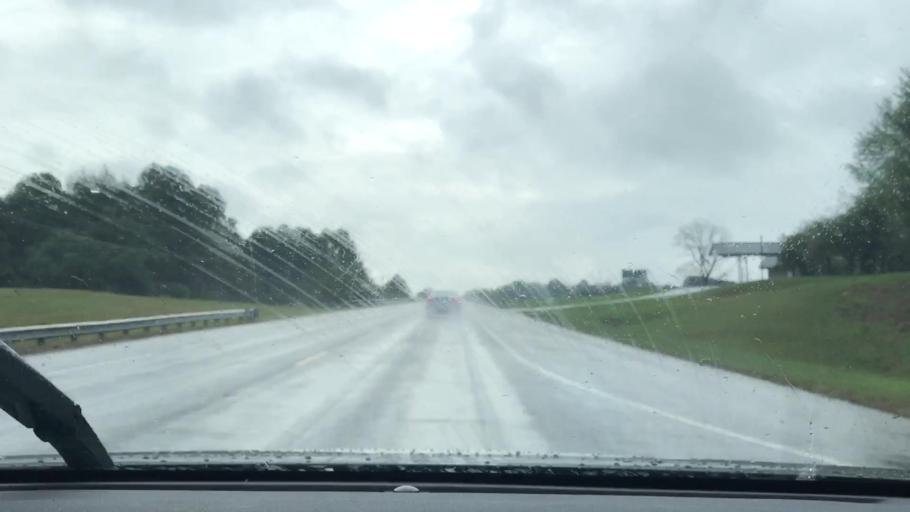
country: US
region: Tennessee
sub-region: Macon County
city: Lafayette
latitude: 36.5297
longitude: -86.1045
